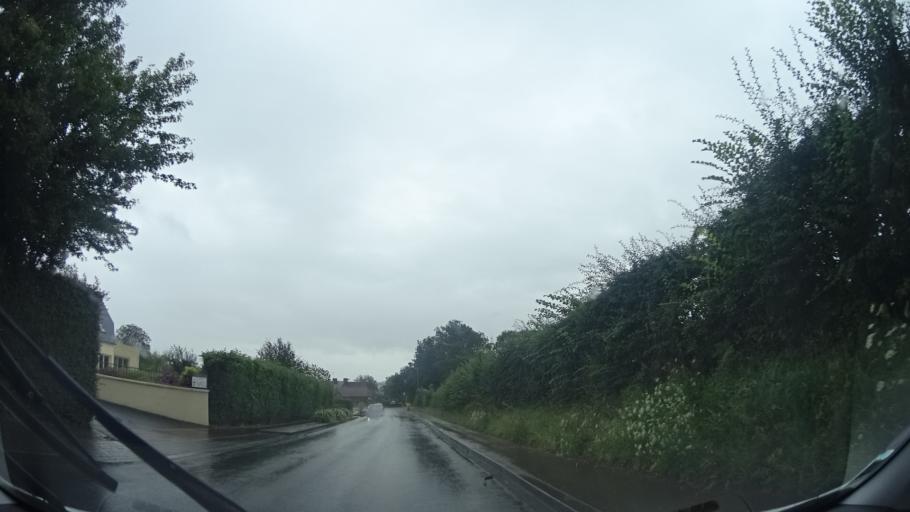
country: FR
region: Lower Normandy
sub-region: Departement de la Manche
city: Beaumont-Hague
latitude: 49.6006
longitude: -1.7808
